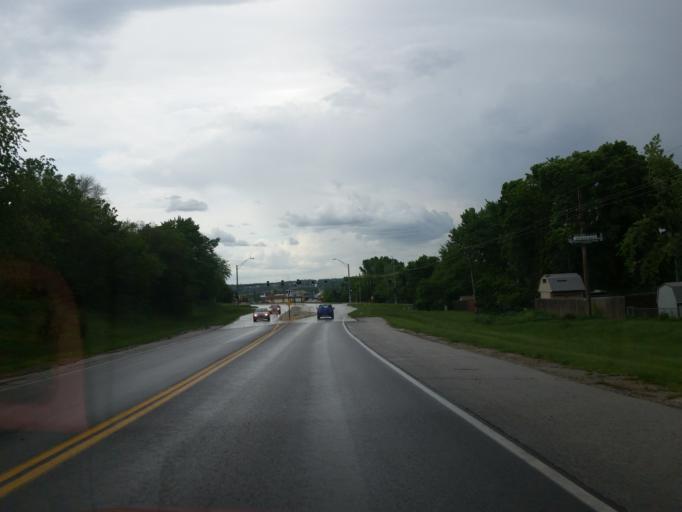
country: US
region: Nebraska
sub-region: Sarpy County
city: Offutt Air Force Base
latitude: 41.1337
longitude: -95.9666
